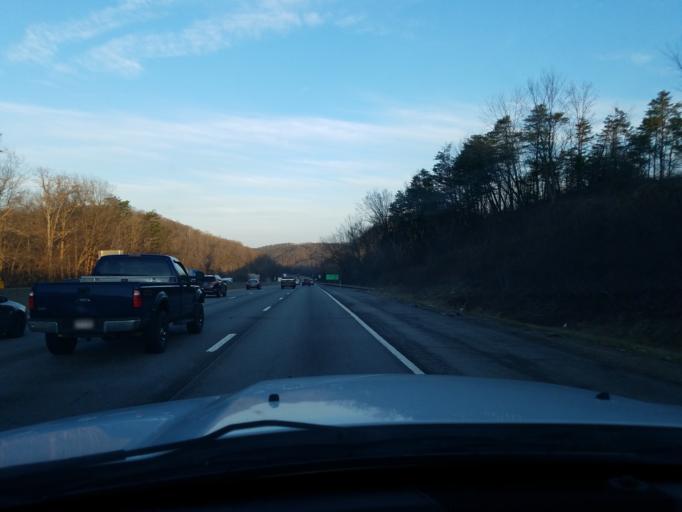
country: US
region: West Virginia
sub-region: Kanawha County
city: Cross Lanes
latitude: 38.4216
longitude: -81.8060
